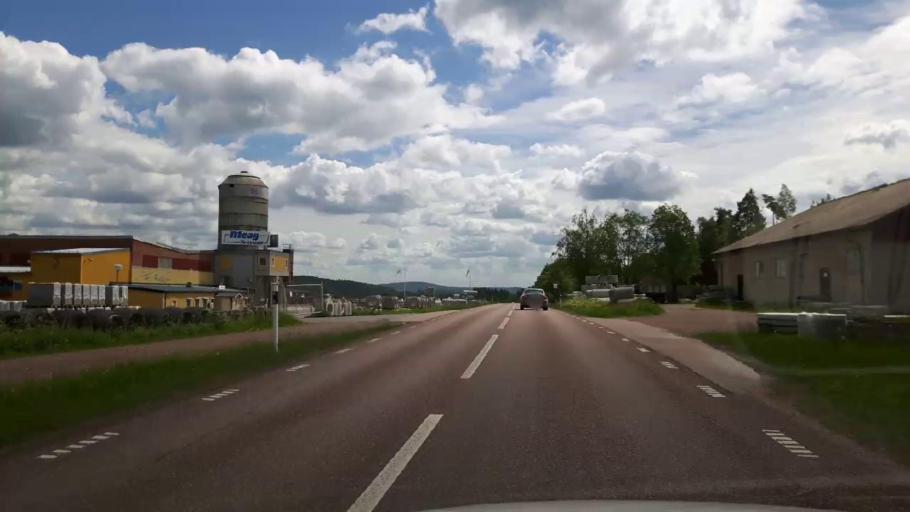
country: SE
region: Dalarna
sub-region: Saters Kommun
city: Saeter
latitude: 60.4284
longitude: 15.8339
